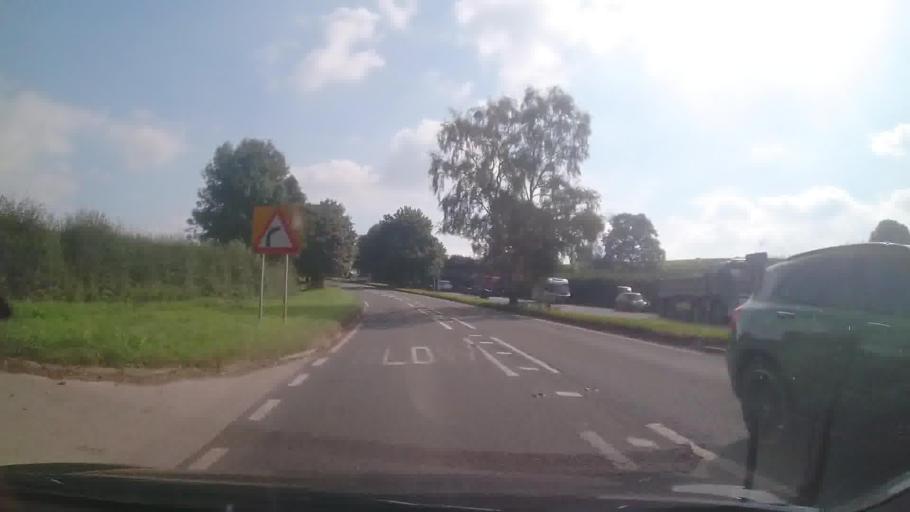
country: GB
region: England
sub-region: Cheshire West and Chester
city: Tiverton
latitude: 53.1300
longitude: -2.6651
